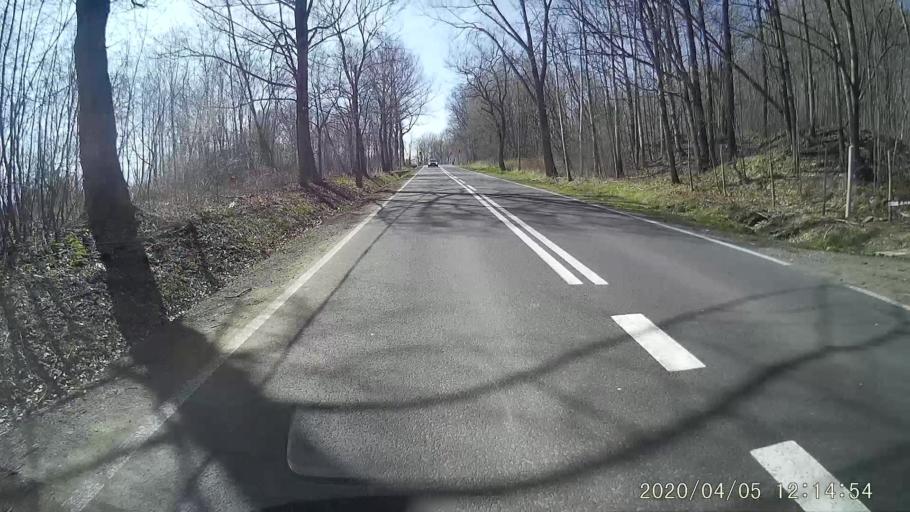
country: PL
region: Lower Silesian Voivodeship
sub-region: Powiat lwowecki
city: Gryfow Slaski
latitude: 51.0177
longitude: 15.3919
